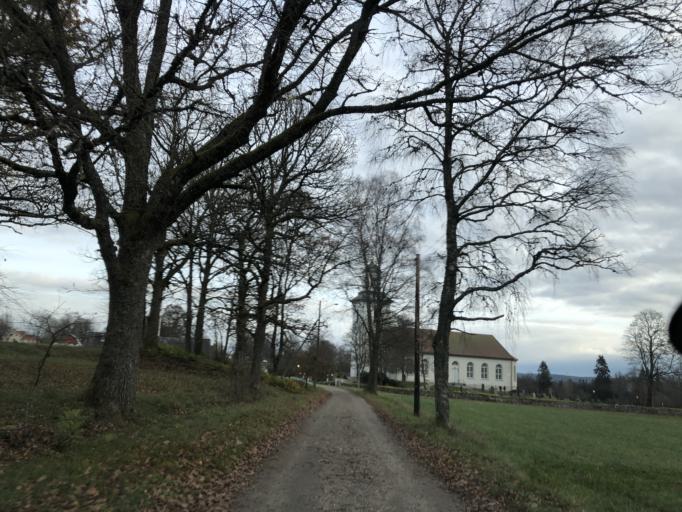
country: SE
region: Vaestra Goetaland
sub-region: Ulricehamns Kommun
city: Ulricehamn
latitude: 57.7251
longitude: 13.3117
